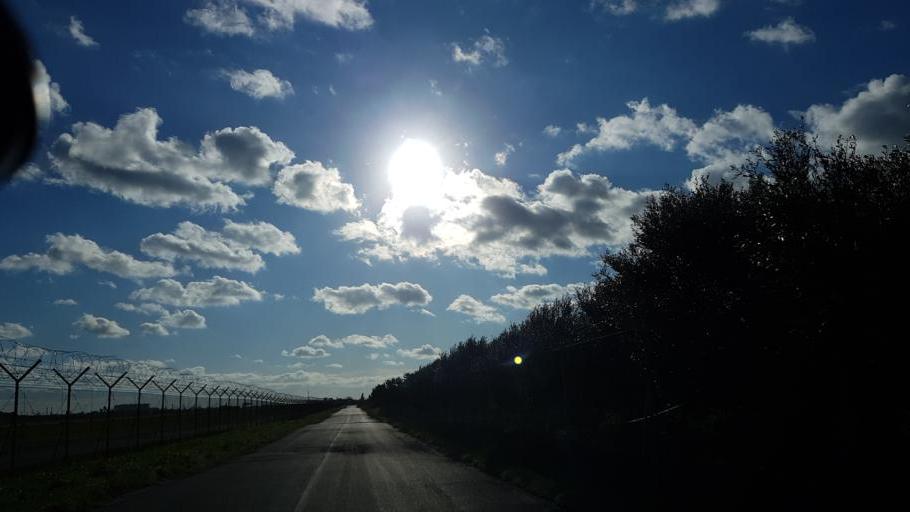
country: IT
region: Apulia
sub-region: Provincia di Brindisi
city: Materdomini
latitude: 40.6637
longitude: 17.9374
